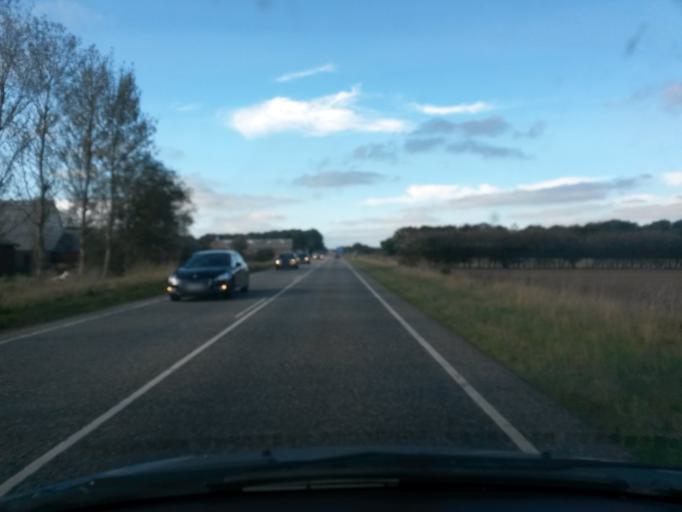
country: DK
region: Central Jutland
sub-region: Holstebro Kommune
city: Holstebro
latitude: 56.3208
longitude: 8.6763
